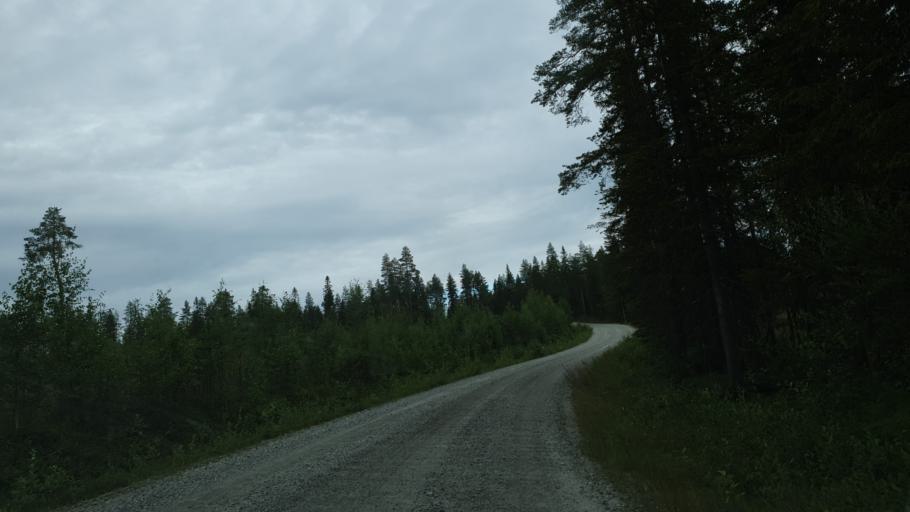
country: FI
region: Kainuu
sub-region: Kehys-Kainuu
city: Kuhmo
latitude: 64.4578
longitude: 29.5790
